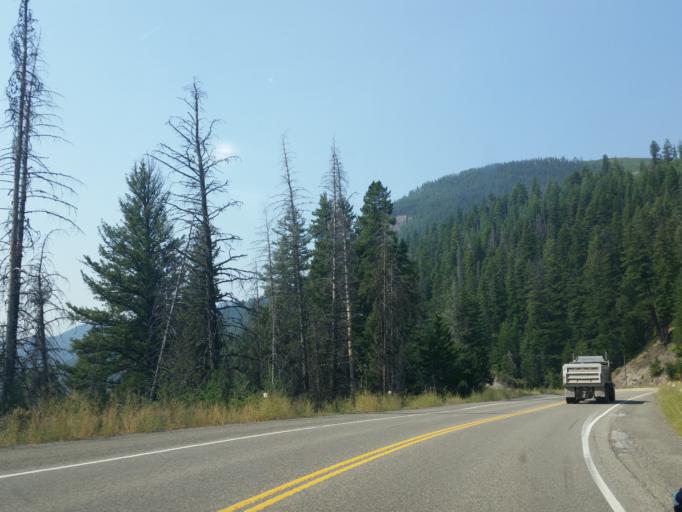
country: CA
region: British Columbia
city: Princeton
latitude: 49.2096
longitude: -120.5522
